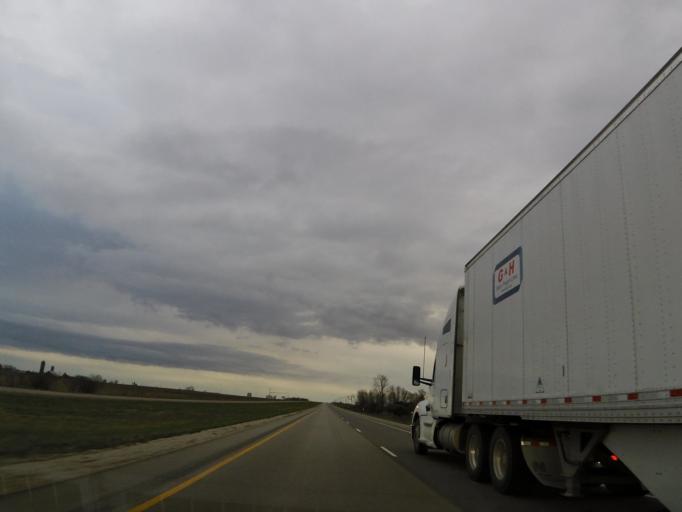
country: US
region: Iowa
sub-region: Henry County
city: Mount Pleasant
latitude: 40.7628
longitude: -91.5641
